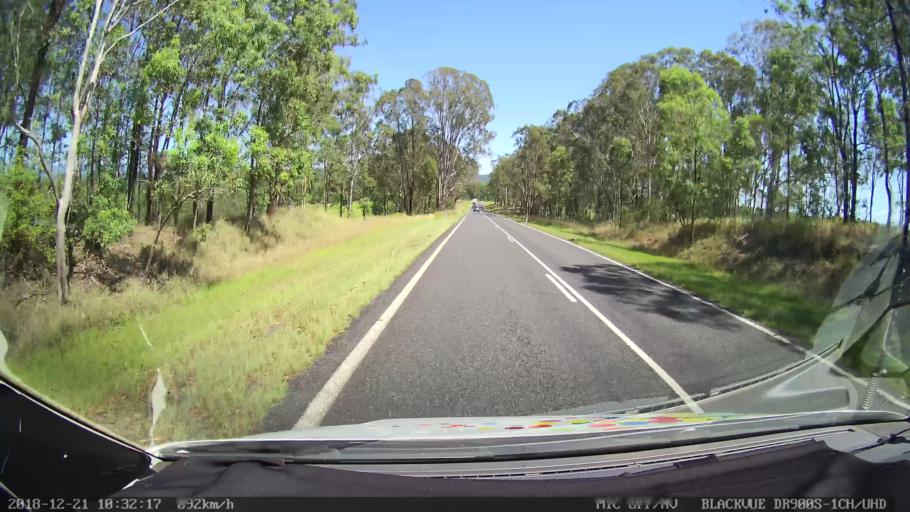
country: AU
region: New South Wales
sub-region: Clarence Valley
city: South Grafton
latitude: -29.6225
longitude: 152.6869
